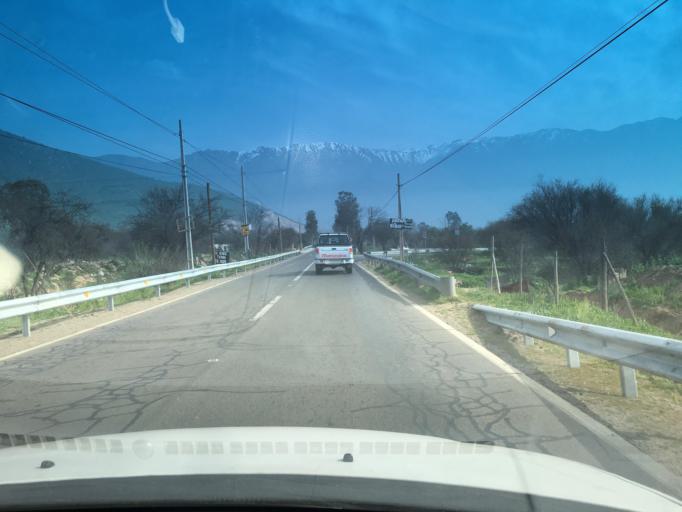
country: CL
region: Santiago Metropolitan
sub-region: Provincia de Chacabuco
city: Lampa
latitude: -33.2487
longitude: -70.9114
